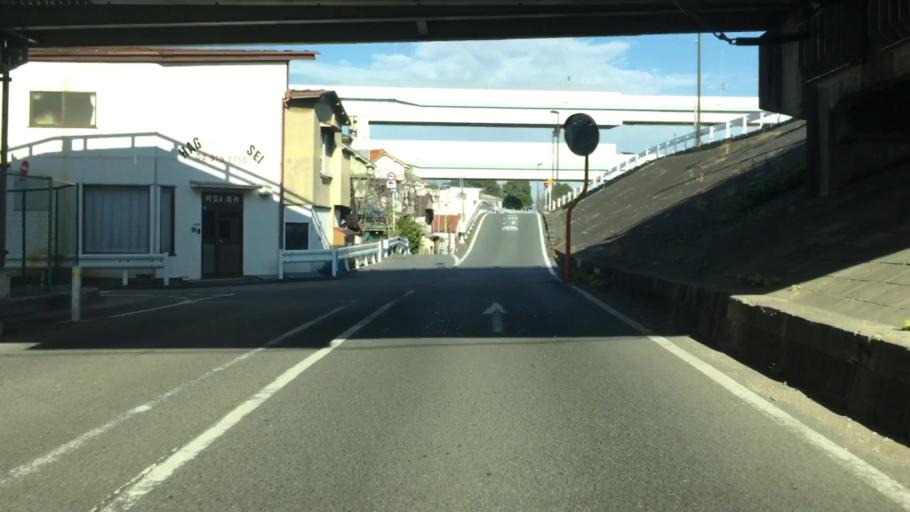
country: JP
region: Saitama
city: Kawaguchi
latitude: 35.7624
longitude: 139.7584
